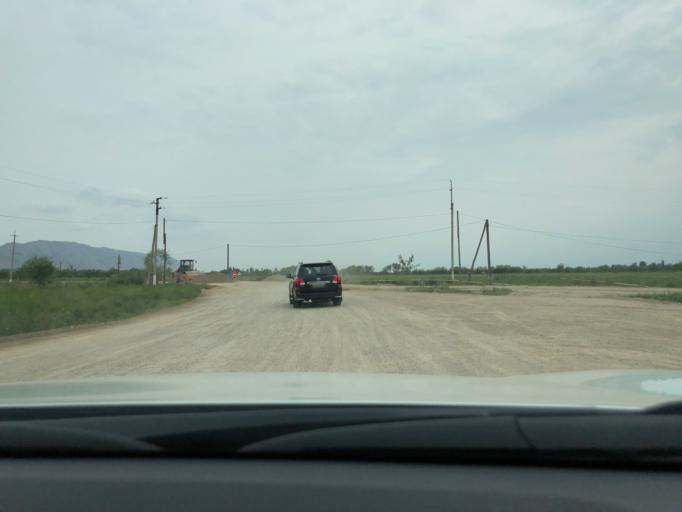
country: TJ
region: Viloyati Sughd
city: Isfara
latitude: 40.1521
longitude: 70.6233
